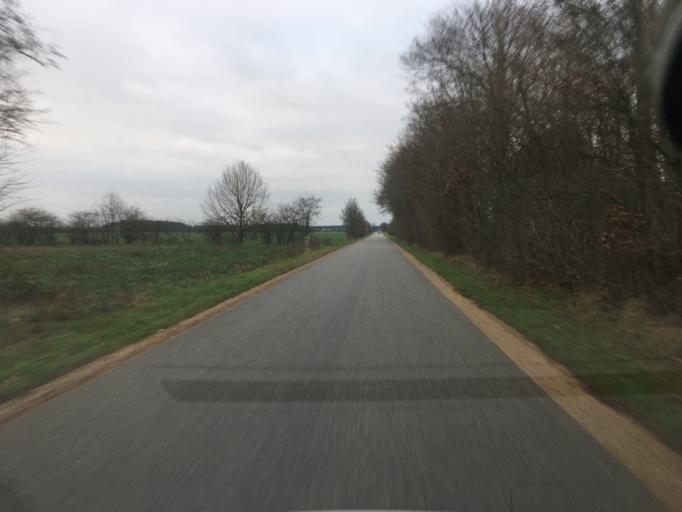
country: DK
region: South Denmark
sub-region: Tonder Kommune
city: Logumkloster
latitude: 55.0360
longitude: 9.0289
